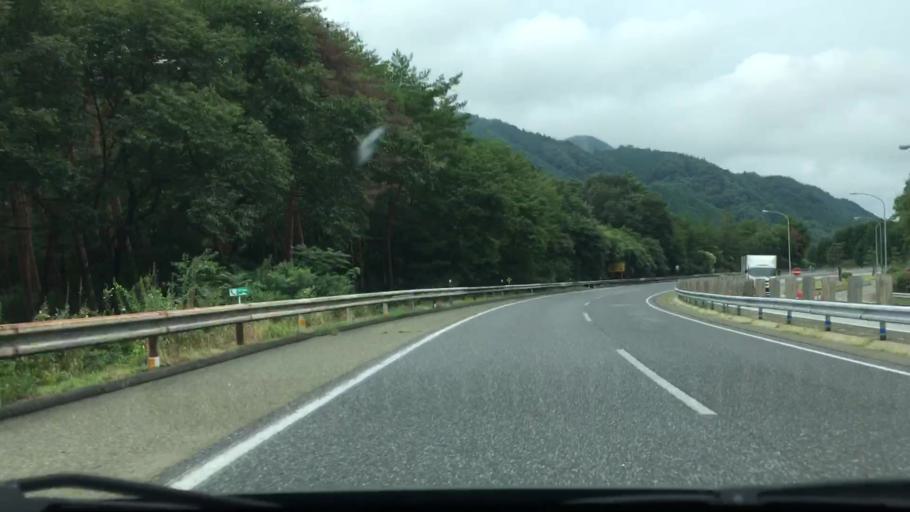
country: JP
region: Hiroshima
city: Shobara
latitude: 34.8566
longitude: 133.1002
